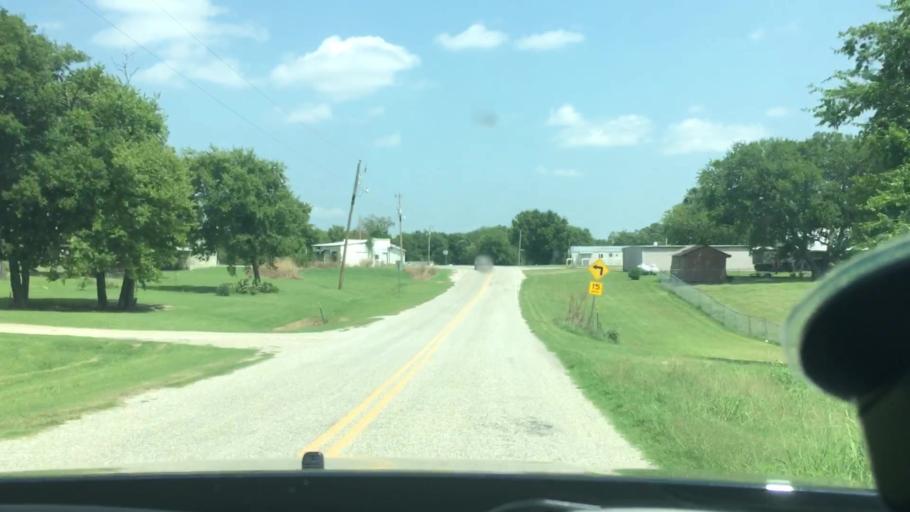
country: US
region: Oklahoma
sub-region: Johnston County
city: Tishomingo
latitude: 34.4184
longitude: -96.4949
